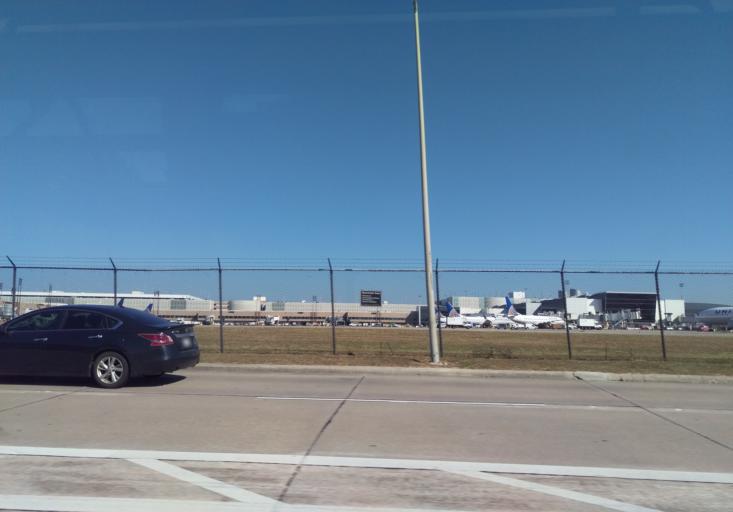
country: US
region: Texas
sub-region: Harris County
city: Aldine
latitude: 29.9817
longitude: -95.3367
